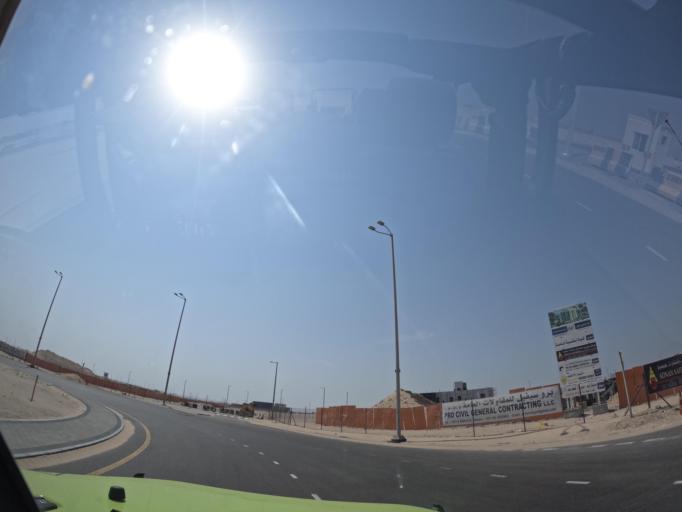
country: AE
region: Abu Dhabi
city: Abu Dhabi
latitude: 24.3693
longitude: 54.6095
